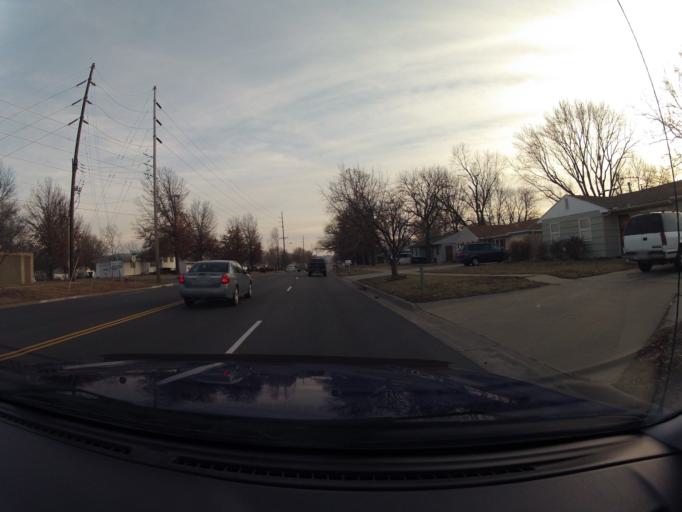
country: US
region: Kansas
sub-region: Shawnee County
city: Topeka
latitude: 39.0357
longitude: -95.7434
